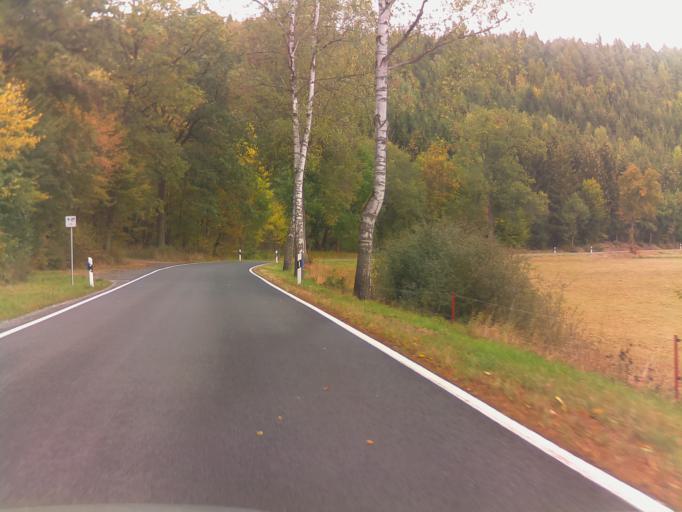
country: DE
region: Thuringia
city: Mehmels
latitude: 50.6473
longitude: 10.3470
